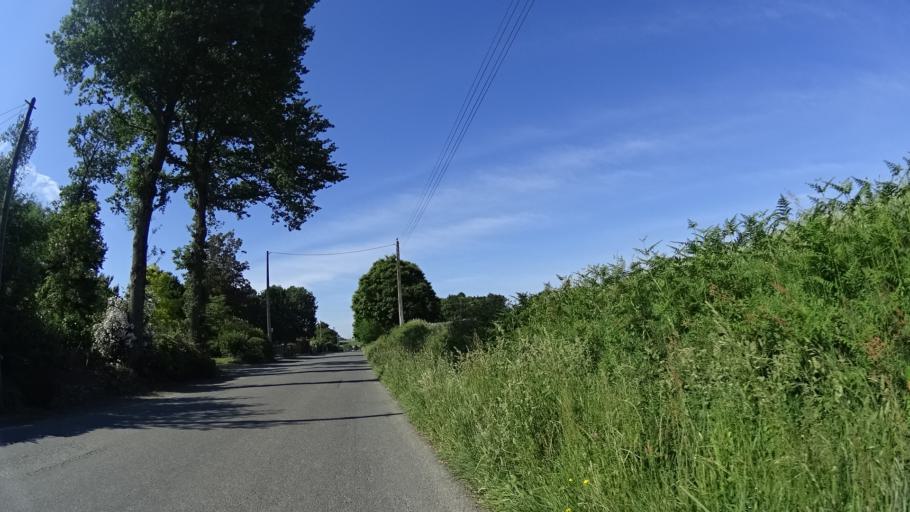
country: FR
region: Brittany
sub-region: Departement d'Ille-et-Vilaine
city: Guipry
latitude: 47.8145
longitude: -1.8495
